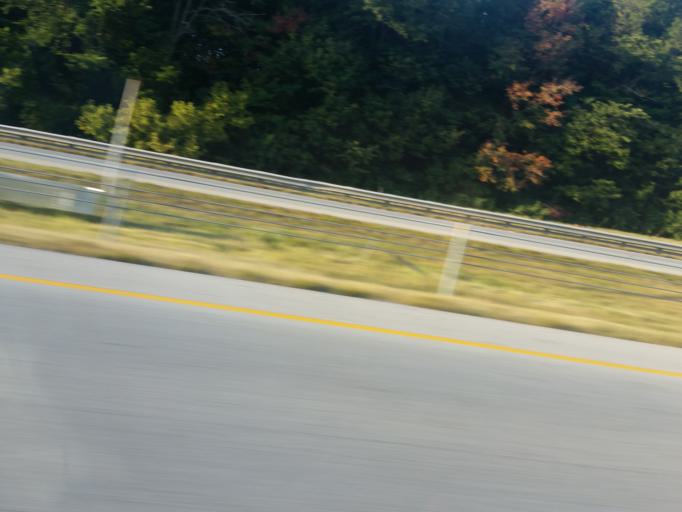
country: US
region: Indiana
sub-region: Boone County
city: Zionsville
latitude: 39.9303
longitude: -86.2708
